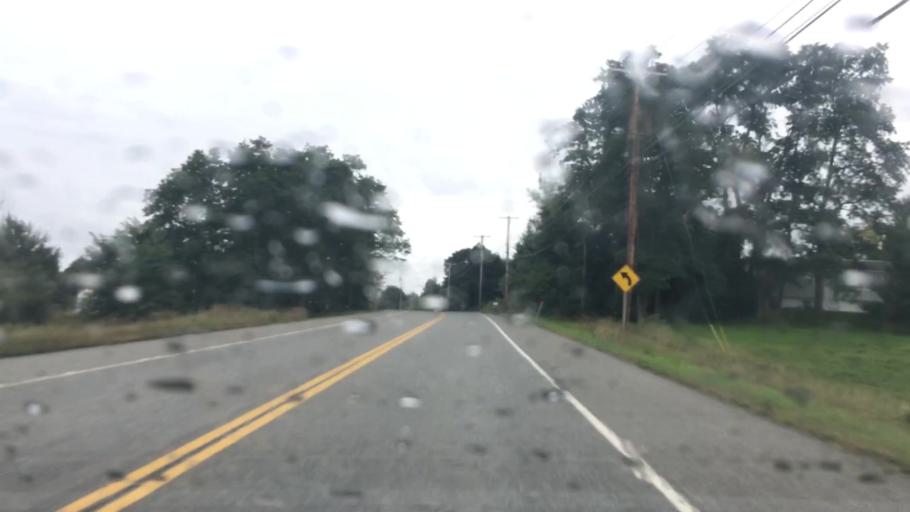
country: US
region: Maine
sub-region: Penobscot County
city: Orrington
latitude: 44.7167
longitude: -68.8271
